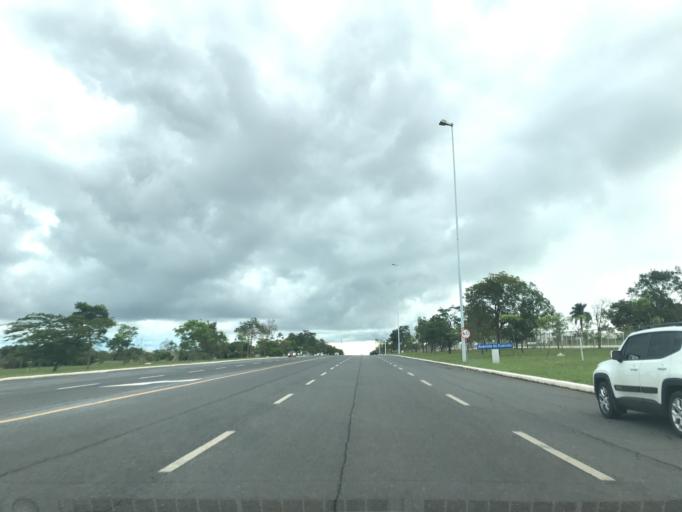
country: BR
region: Federal District
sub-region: Brasilia
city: Brasilia
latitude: -15.7647
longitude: -47.9172
